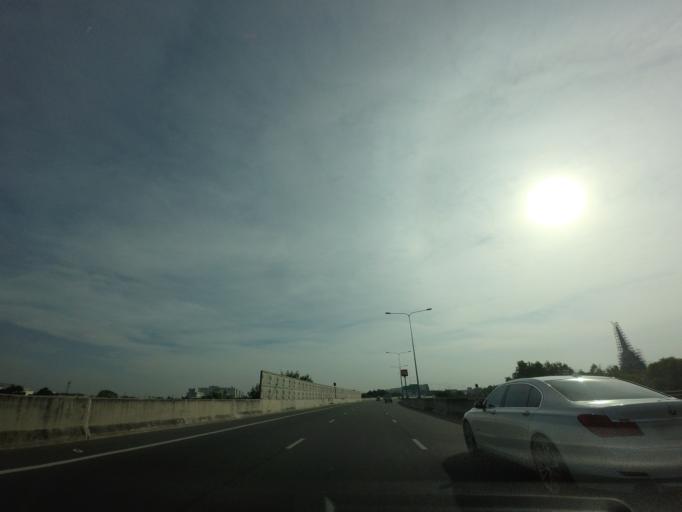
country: TH
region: Bangkok
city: Bang Khen
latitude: 13.8628
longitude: 100.6450
